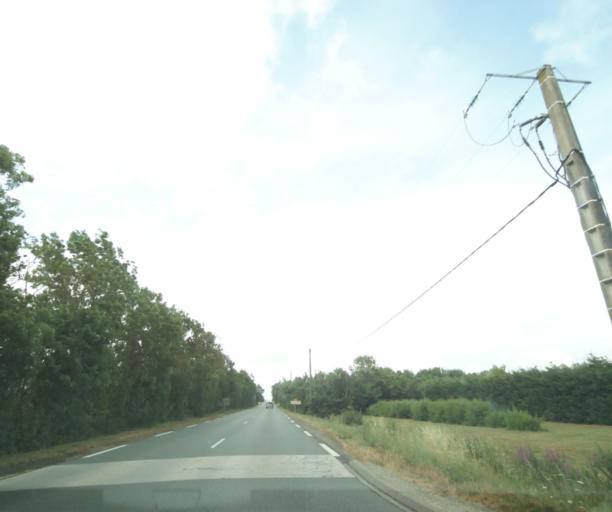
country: FR
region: Poitou-Charentes
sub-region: Departement de la Charente-Maritime
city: Charron
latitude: 46.3006
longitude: -1.0871
